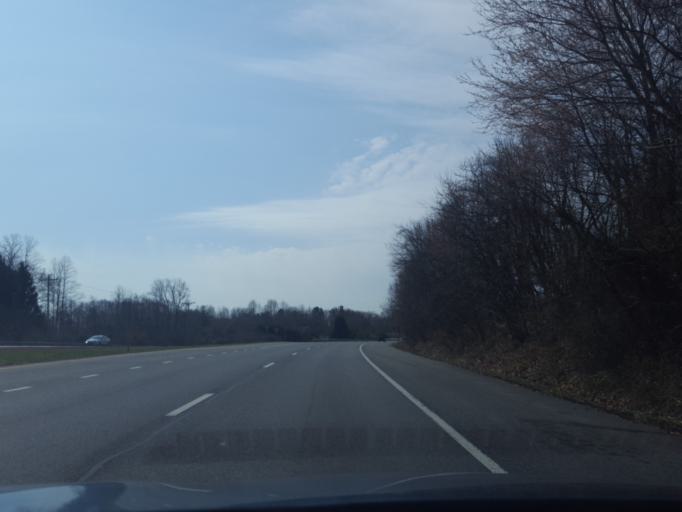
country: US
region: Maryland
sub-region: Calvert County
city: Dunkirk
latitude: 38.7601
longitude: -76.6572
